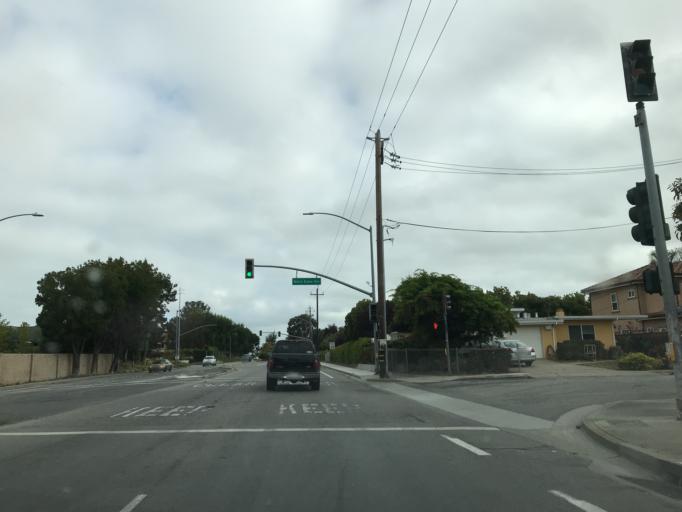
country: US
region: California
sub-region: San Mateo County
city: East Palo Alto
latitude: 37.4756
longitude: -122.1395
